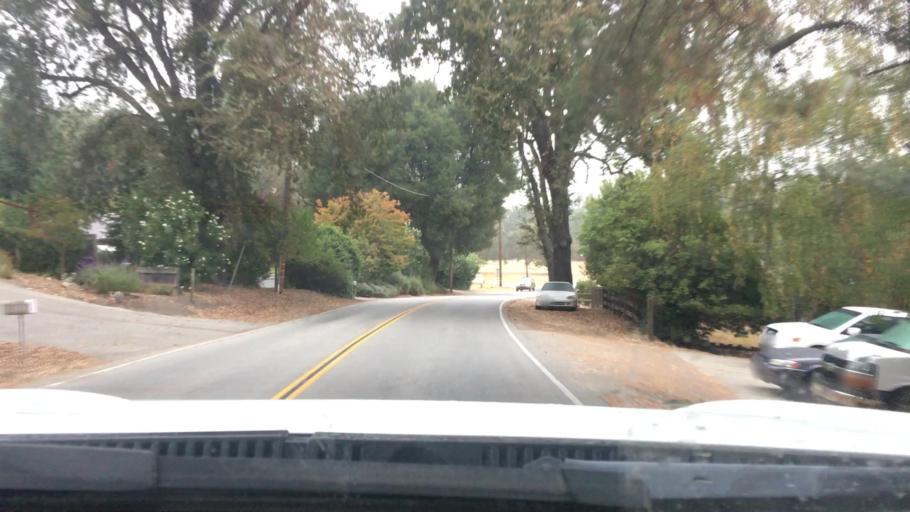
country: US
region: California
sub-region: San Luis Obispo County
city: Atascadero
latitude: 35.4915
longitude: -120.6841
